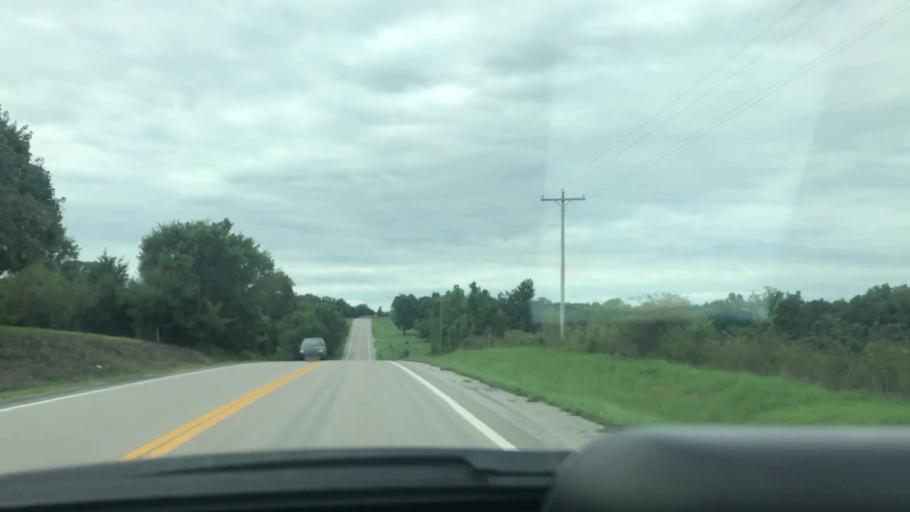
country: US
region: Missouri
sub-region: Benton County
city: Warsaw
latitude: 38.1488
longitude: -93.2926
